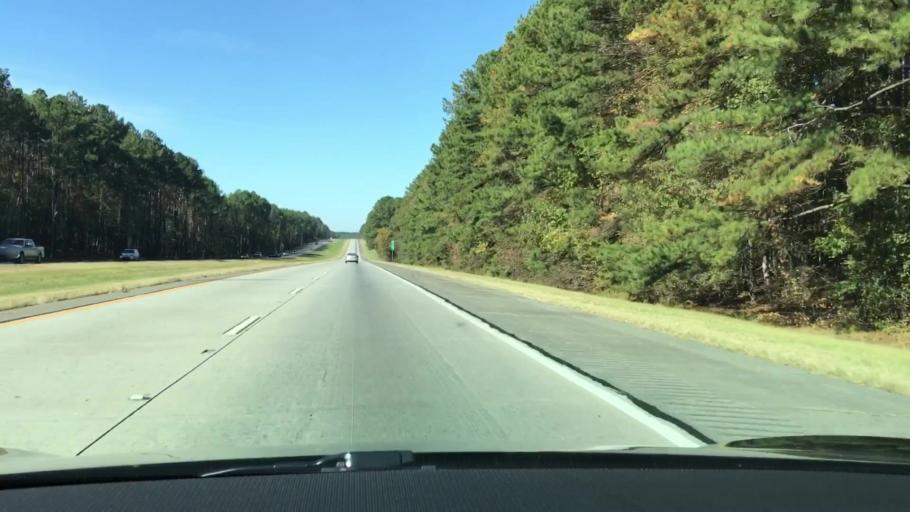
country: US
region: Georgia
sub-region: Taliaferro County
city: Crawfordville
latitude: 33.5247
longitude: -82.8784
